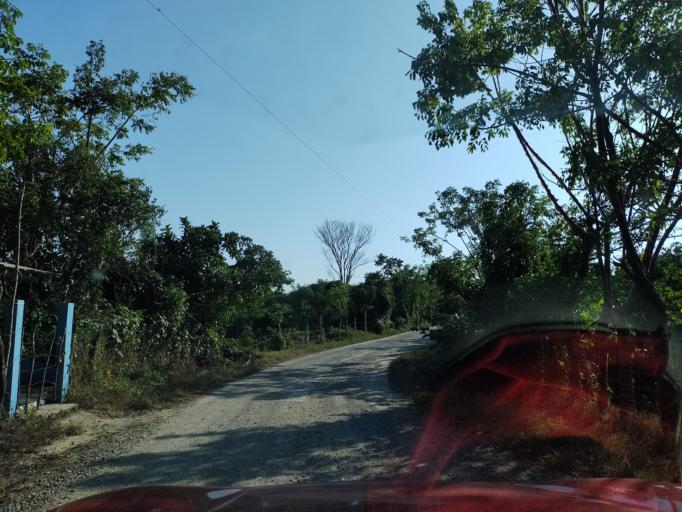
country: MX
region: Veracruz
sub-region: Papantla
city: Polutla
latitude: 20.4504
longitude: -97.2422
